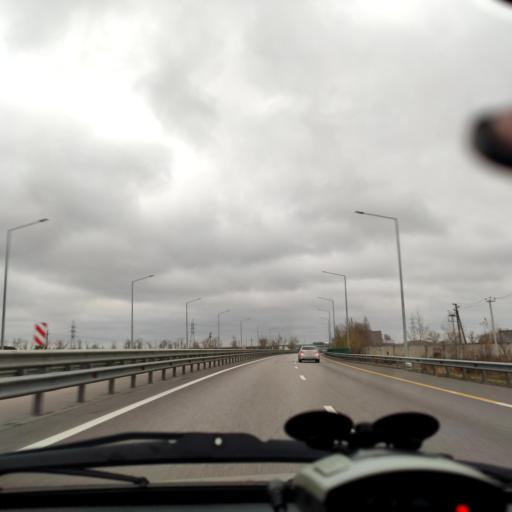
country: RU
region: Voronezj
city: Novaya Usman'
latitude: 51.6324
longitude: 39.3174
